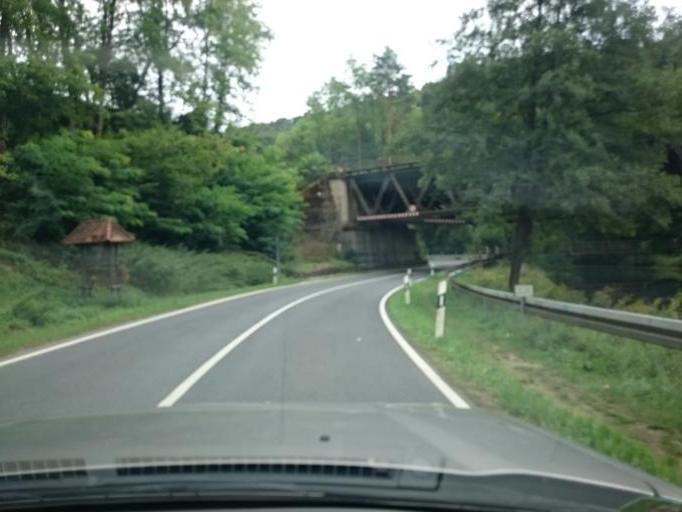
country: DE
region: Bavaria
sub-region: Regierungsbezirk Mittelfranken
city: Velden
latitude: 49.6105
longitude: 11.5160
